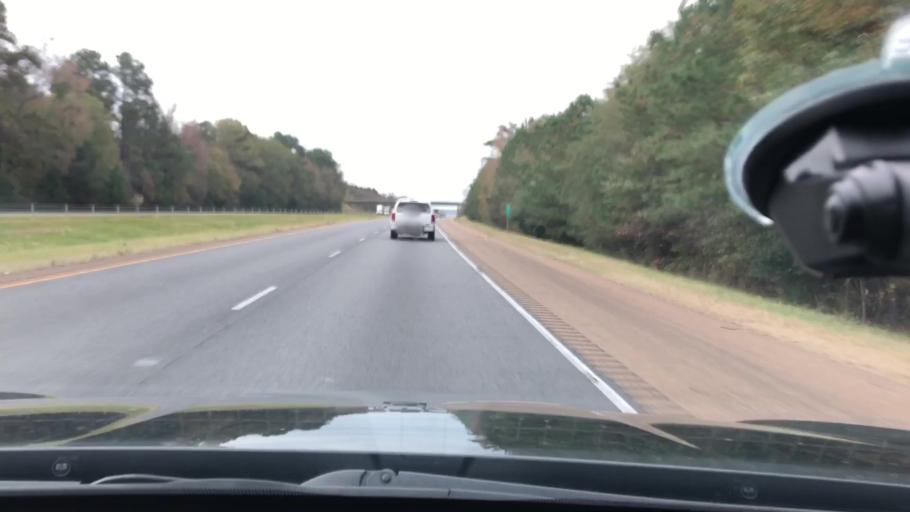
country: US
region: Arkansas
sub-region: Nevada County
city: Prescott
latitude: 33.8783
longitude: -93.3308
